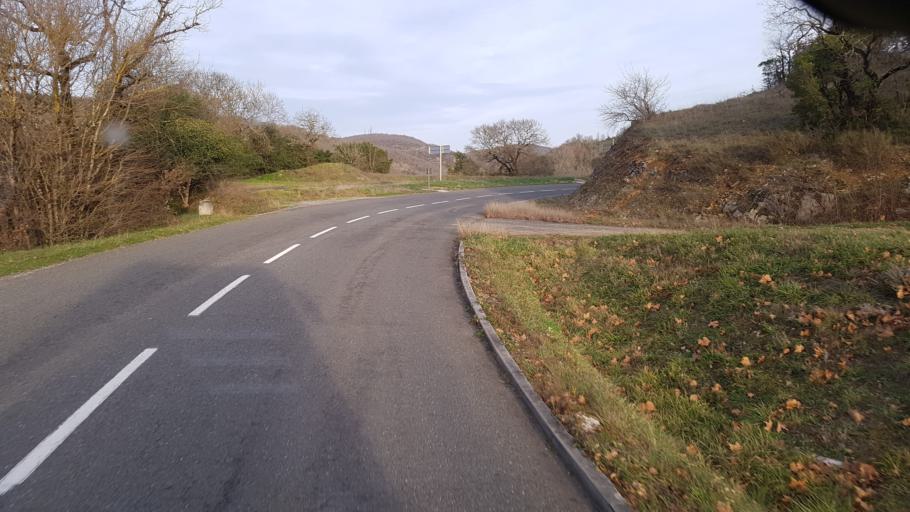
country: FR
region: Midi-Pyrenees
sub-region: Departement du Tarn-et-Garonne
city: Montricoux
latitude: 44.0156
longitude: 1.6768
